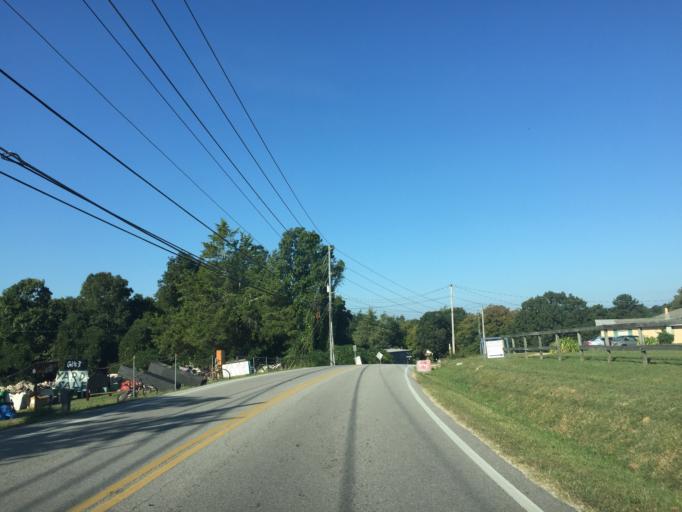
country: US
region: Tennessee
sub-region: Hamilton County
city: Harrison
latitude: 35.1208
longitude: -85.1075
